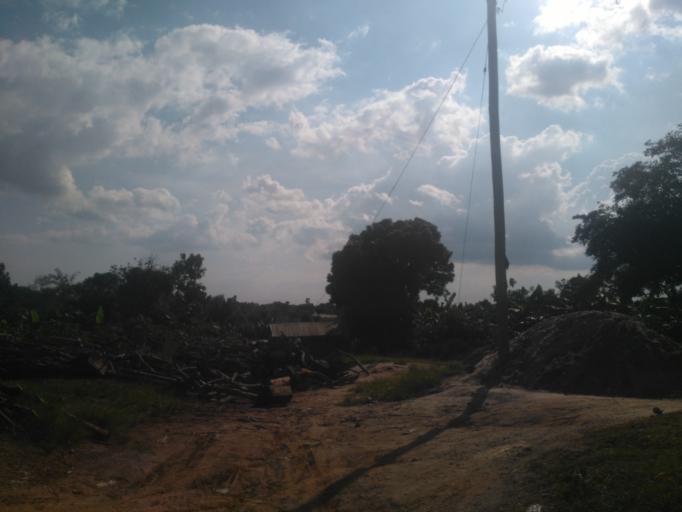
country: UG
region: Central Region
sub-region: Wakiso District
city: Wakiso
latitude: 0.2972
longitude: 32.4508
